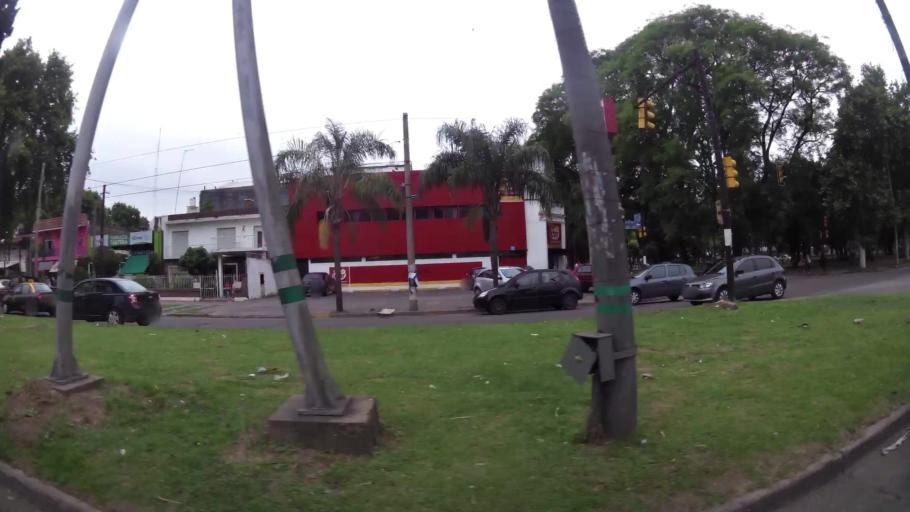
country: AR
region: Santa Fe
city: Granadero Baigorria
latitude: -32.8941
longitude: -60.6924
